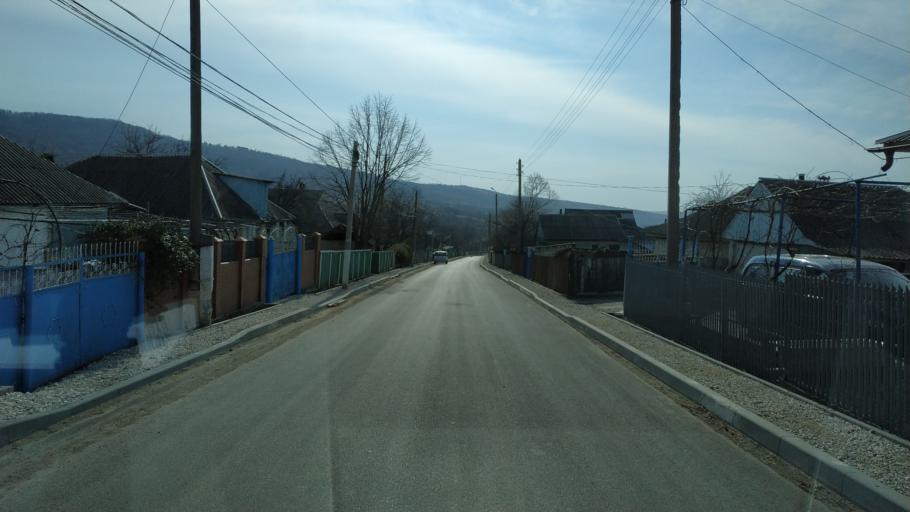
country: MD
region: Nisporeni
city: Nisporeni
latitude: 47.1610
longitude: 28.1345
